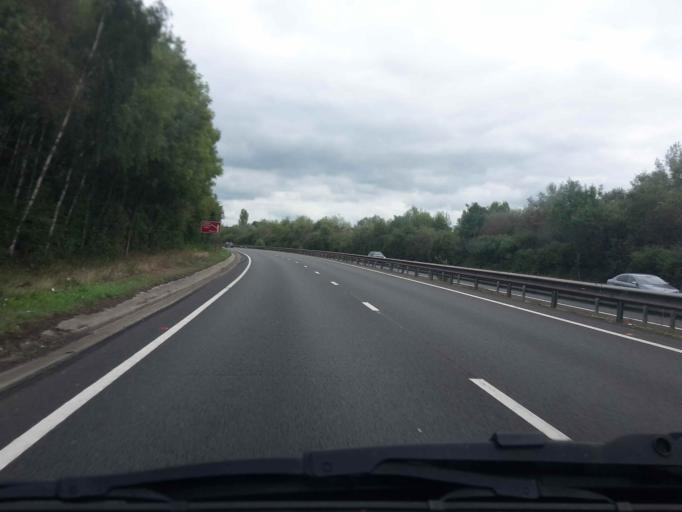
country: GB
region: England
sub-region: Surrey
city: Seale
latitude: 51.2509
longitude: -0.7308
